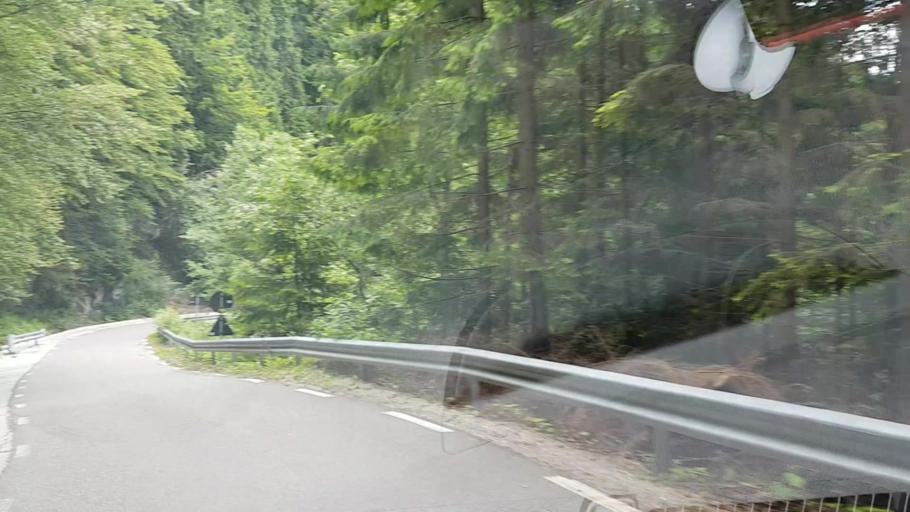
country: RO
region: Suceava
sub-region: Comuna Crucea
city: Crucea
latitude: 47.4353
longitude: 25.5724
